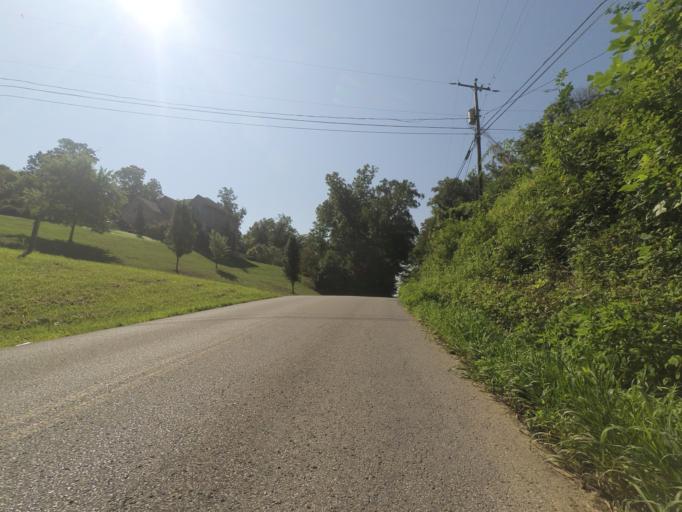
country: US
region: West Virginia
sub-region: Cabell County
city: Huntington
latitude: 38.4366
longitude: -82.4322
